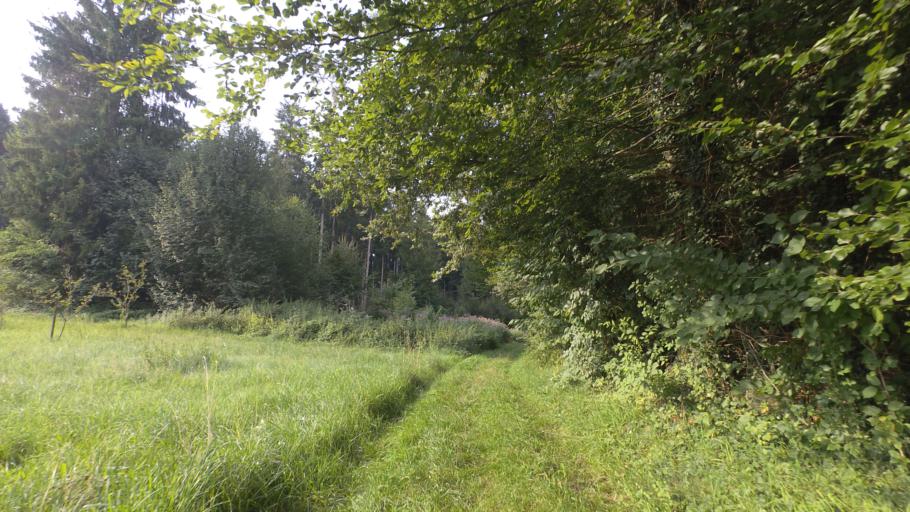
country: DE
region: Bavaria
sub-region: Upper Bavaria
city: Chieming
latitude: 47.9155
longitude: 12.5611
